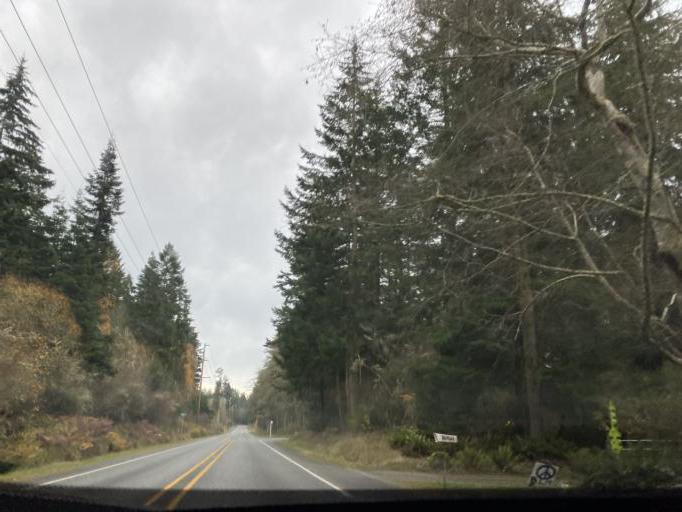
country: US
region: Washington
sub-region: Island County
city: Freeland
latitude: 48.0345
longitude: -122.5940
